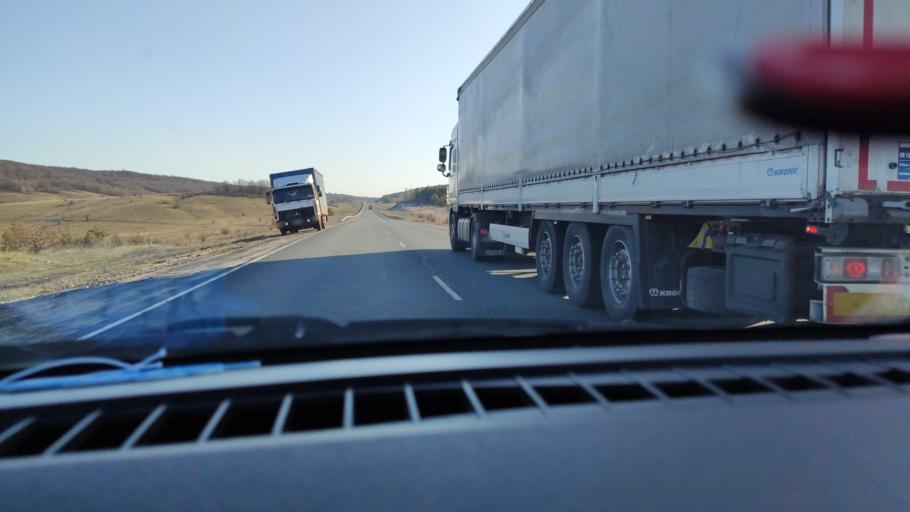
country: RU
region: Saratov
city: Alekseyevka
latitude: 52.3990
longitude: 47.9872
